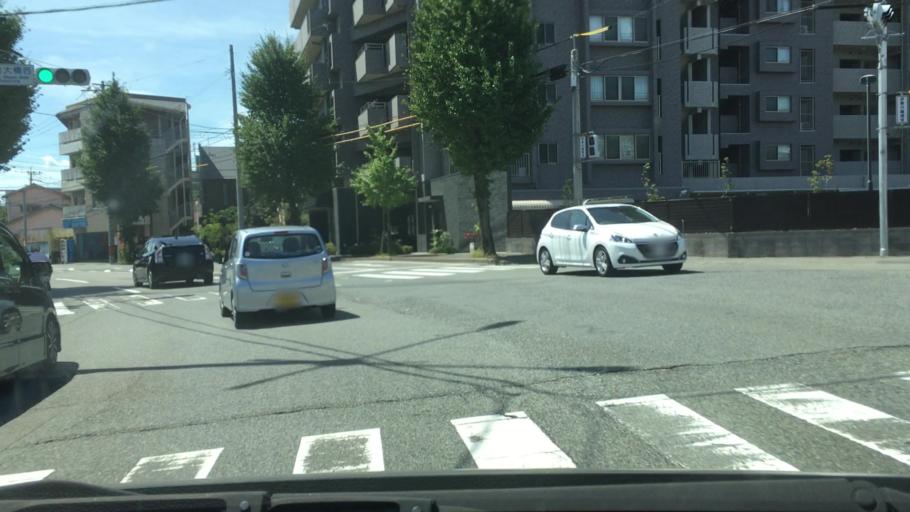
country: JP
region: Fukuoka
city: Fukuoka-shi
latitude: 33.5736
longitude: 130.4215
